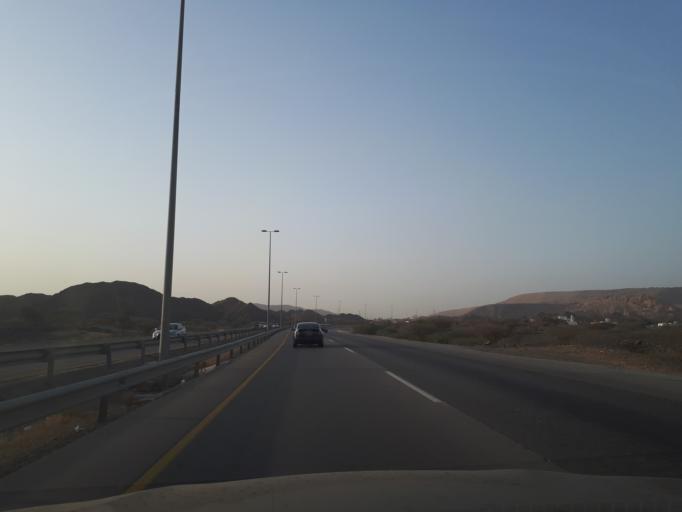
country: OM
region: Muhafazat ad Dakhiliyah
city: Bidbid
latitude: 23.5117
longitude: 58.1920
